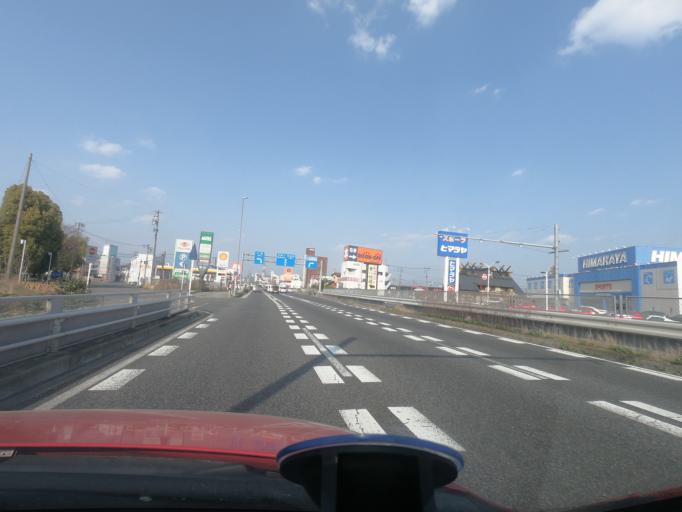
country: JP
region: Aichi
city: Kasugai
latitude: 35.2585
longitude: 136.9836
